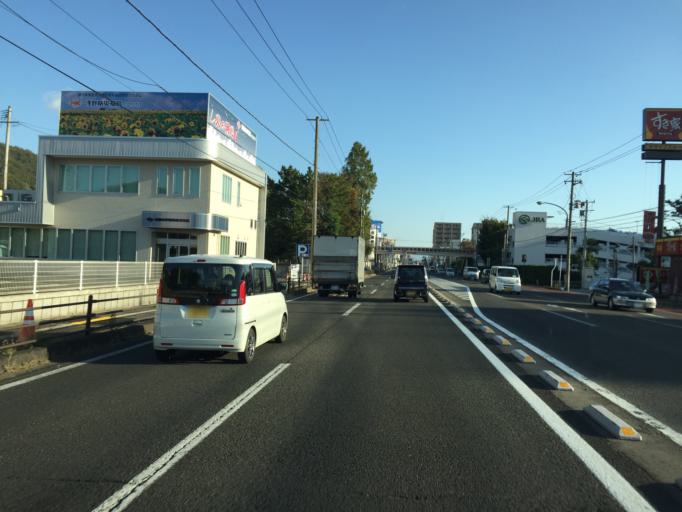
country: JP
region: Fukushima
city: Fukushima-shi
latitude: 37.7652
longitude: 140.4784
